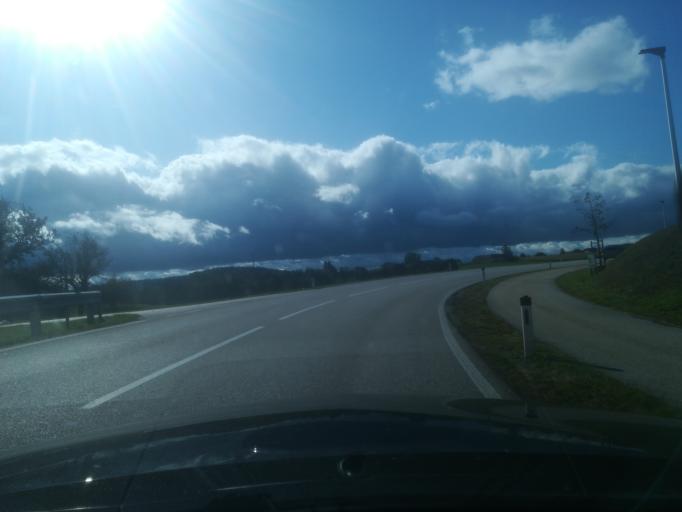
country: AT
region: Upper Austria
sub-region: Politischer Bezirk Urfahr-Umgebung
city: Eidenberg
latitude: 48.3616
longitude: 14.2543
